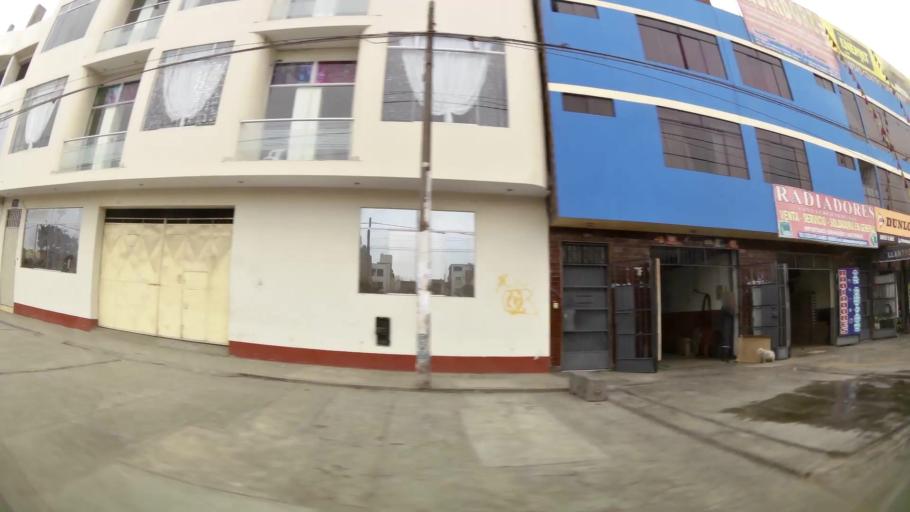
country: PE
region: Lima
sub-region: Lima
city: Independencia
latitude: -11.9601
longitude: -77.0609
